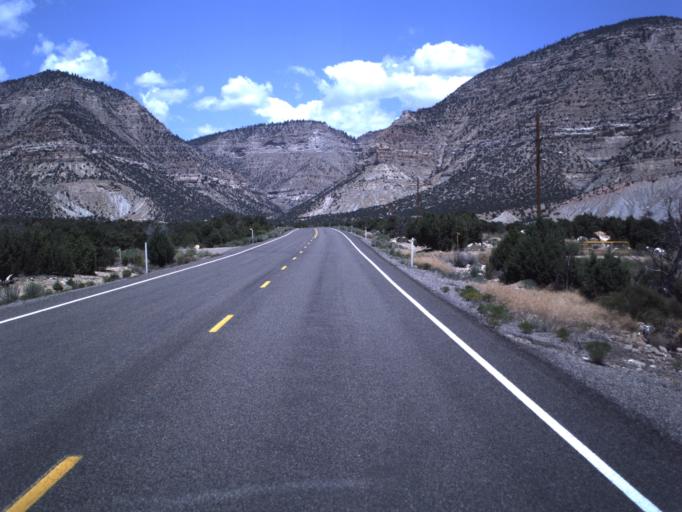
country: US
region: Utah
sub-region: Emery County
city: Orangeville
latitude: 39.2915
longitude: -111.1103
